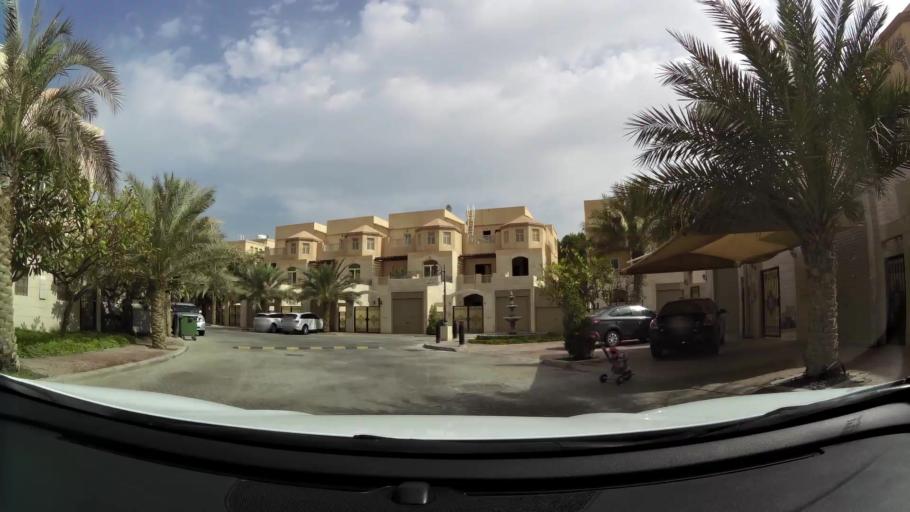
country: AE
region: Abu Dhabi
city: Abu Dhabi
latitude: 24.4437
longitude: 54.3719
